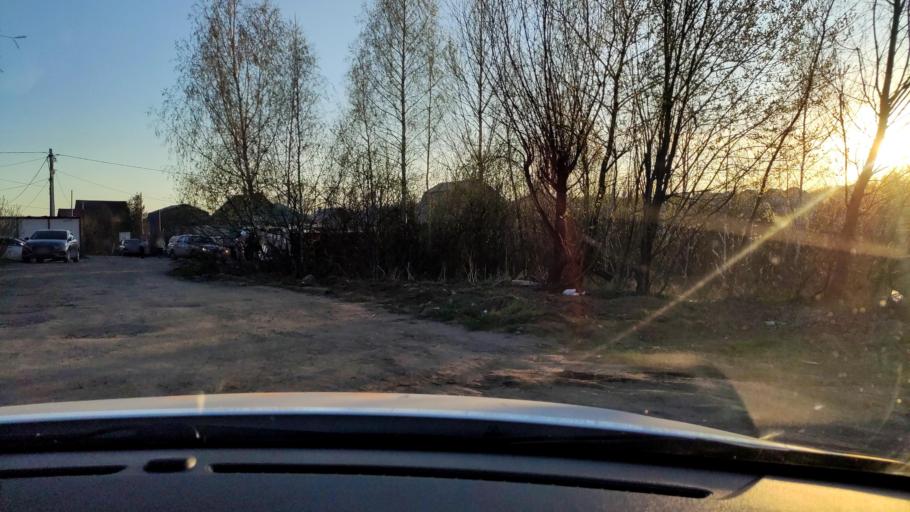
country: RU
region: Tatarstan
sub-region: Gorod Kazan'
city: Kazan
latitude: 55.9097
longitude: 49.1670
